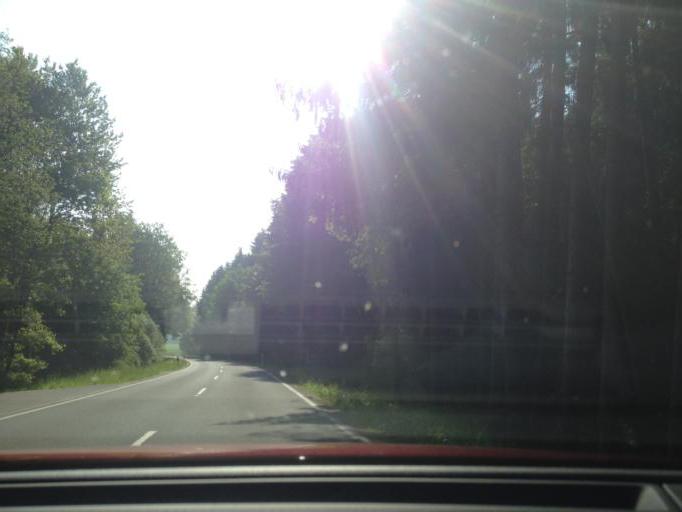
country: DE
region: Bavaria
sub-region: Upper Palatinate
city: Speinshart
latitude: 49.7776
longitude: 11.7915
